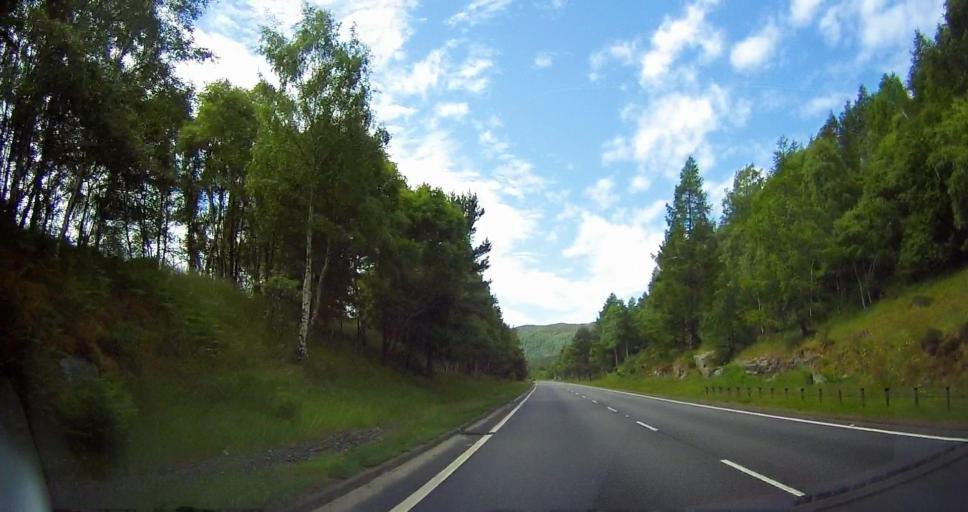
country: GB
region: Scotland
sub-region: Highland
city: Aviemore
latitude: 57.2086
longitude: -3.8293
